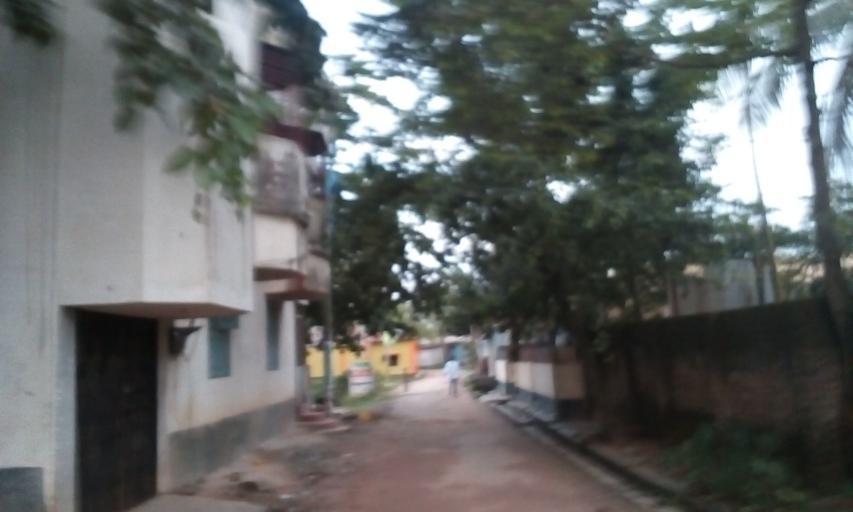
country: IN
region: West Bengal
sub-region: Dakshin Dinajpur
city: Balurghat
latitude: 25.3835
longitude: 88.9927
